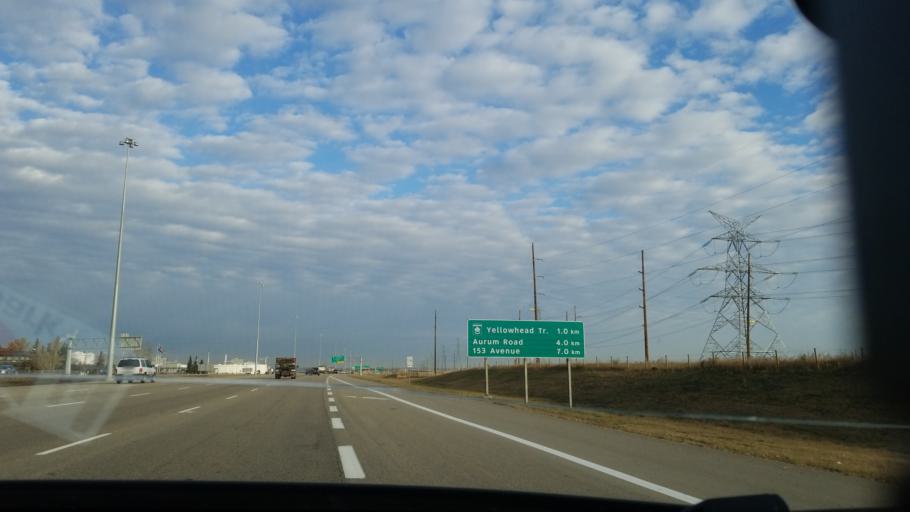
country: CA
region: Alberta
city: Sherwood Park
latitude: 53.5485
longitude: -113.3434
